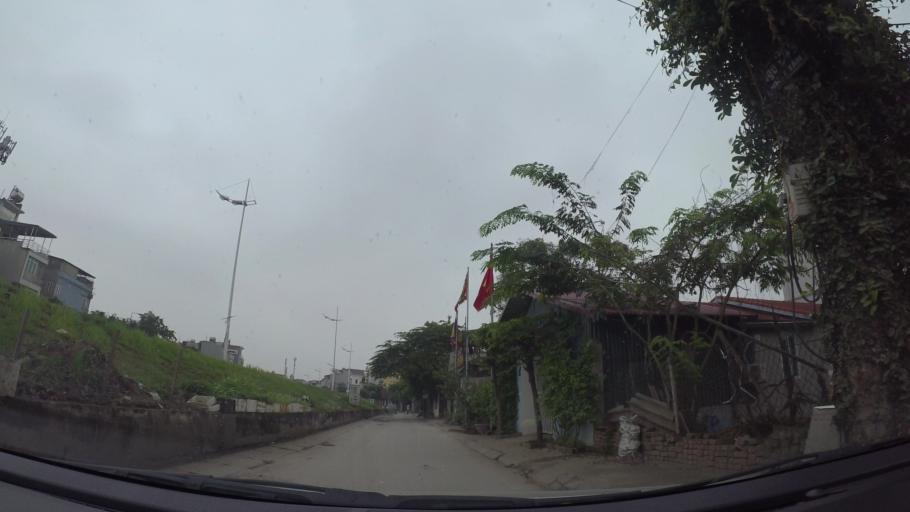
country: VN
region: Ha Noi
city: Tay Ho
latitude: 21.0715
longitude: 105.8276
